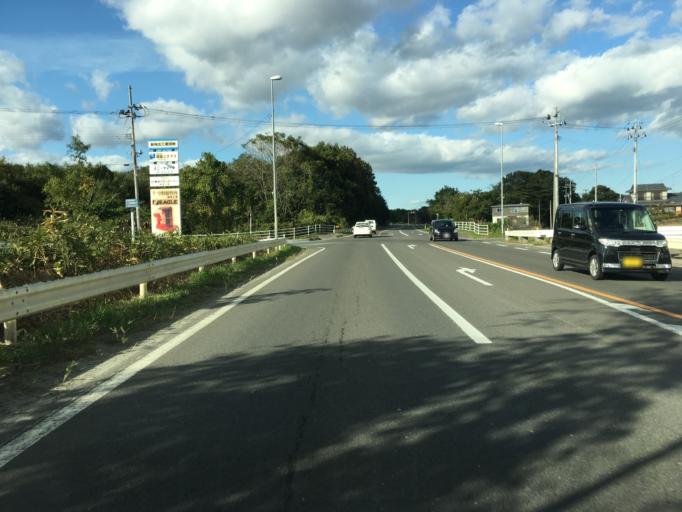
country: JP
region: Miyagi
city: Marumori
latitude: 37.9025
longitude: 140.9003
